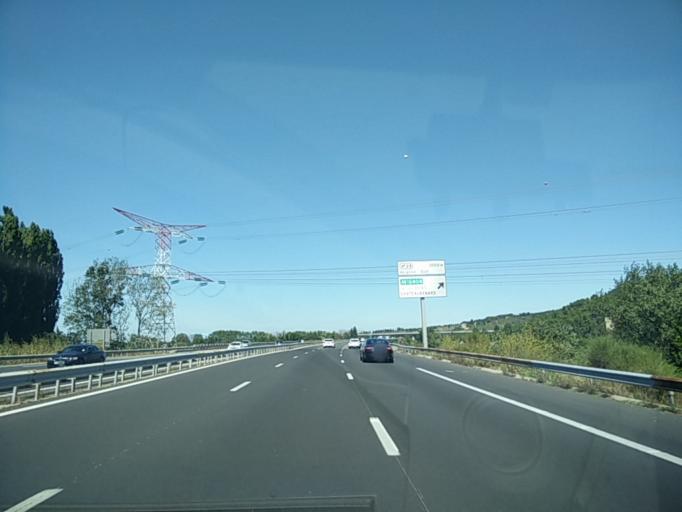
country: FR
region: Provence-Alpes-Cote d'Azur
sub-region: Departement des Bouches-du-Rhone
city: Noves
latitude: 43.8836
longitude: 4.9243
